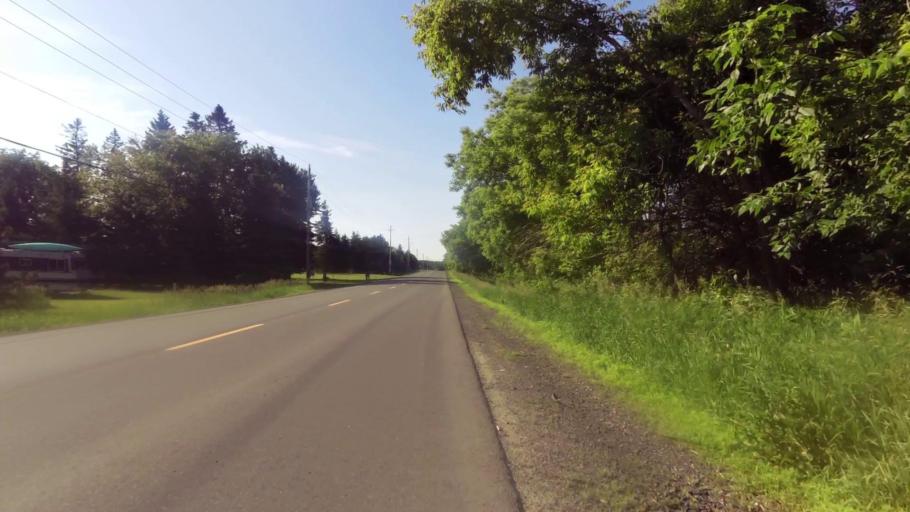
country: CA
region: Ontario
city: Ottawa
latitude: 45.2514
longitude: -75.5643
